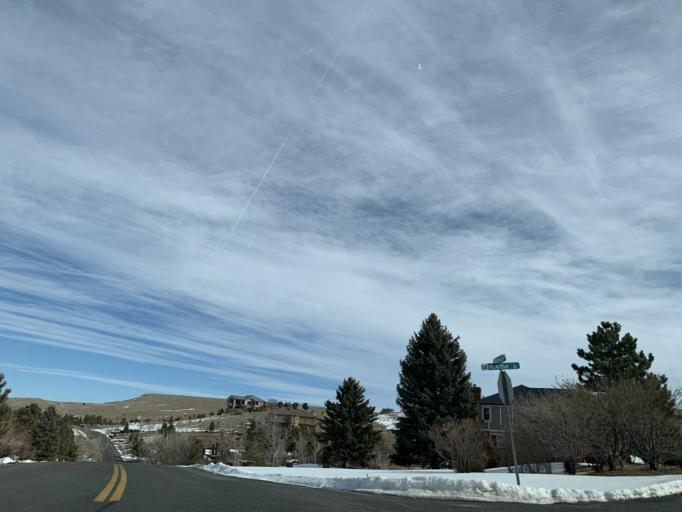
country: US
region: Colorado
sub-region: Douglas County
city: Carriage Club
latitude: 39.5155
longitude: -104.8999
